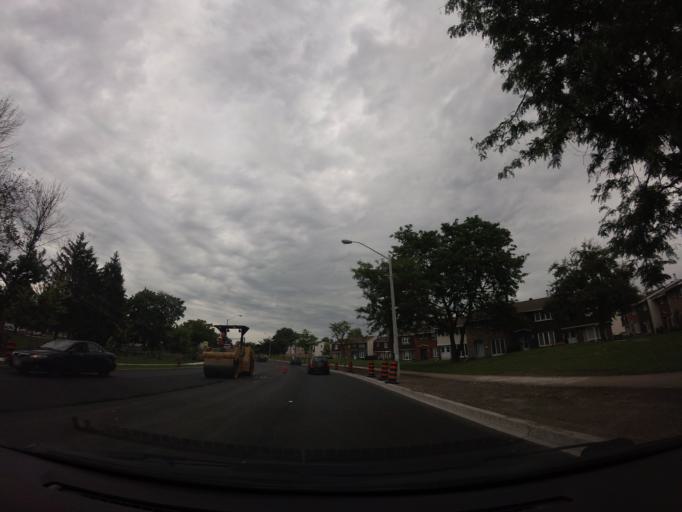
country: CA
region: Ontario
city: Ottawa
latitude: 45.4405
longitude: -75.5975
